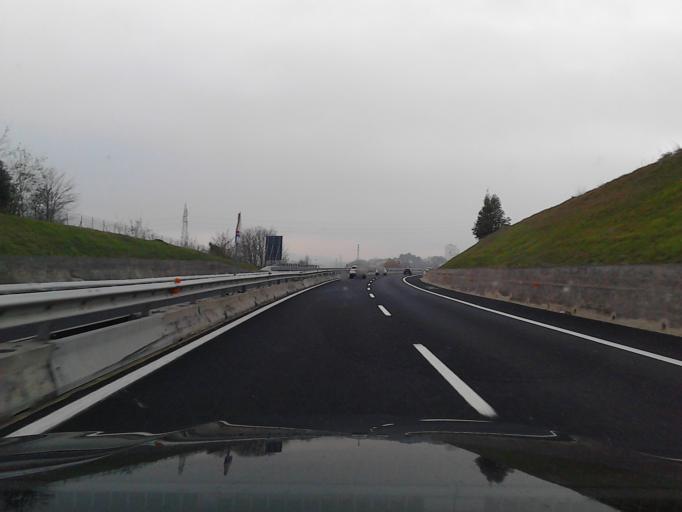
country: IT
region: Abruzzo
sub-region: Provincia di Pescara
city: San Martino Bassa
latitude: 42.5102
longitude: 14.1237
